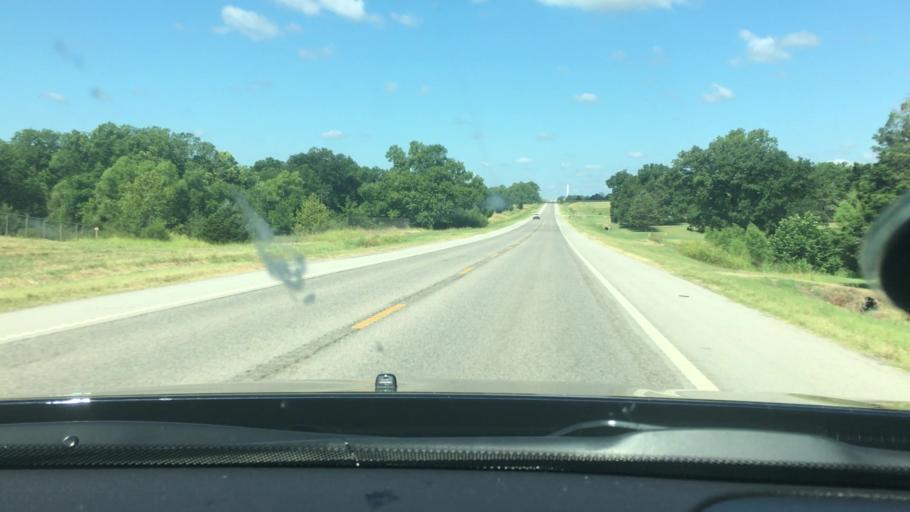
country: US
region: Oklahoma
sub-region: Carter County
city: Dickson
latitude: 34.1003
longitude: -96.9196
